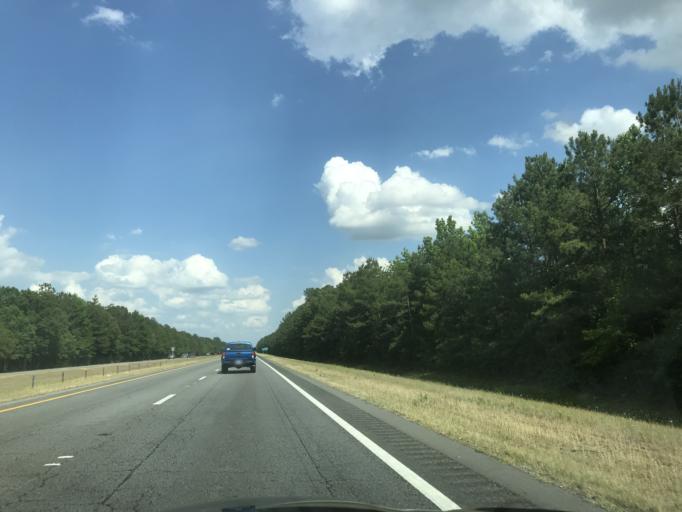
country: US
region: North Carolina
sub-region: Nash County
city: Rocky Mount
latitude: 35.9314
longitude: -77.7039
